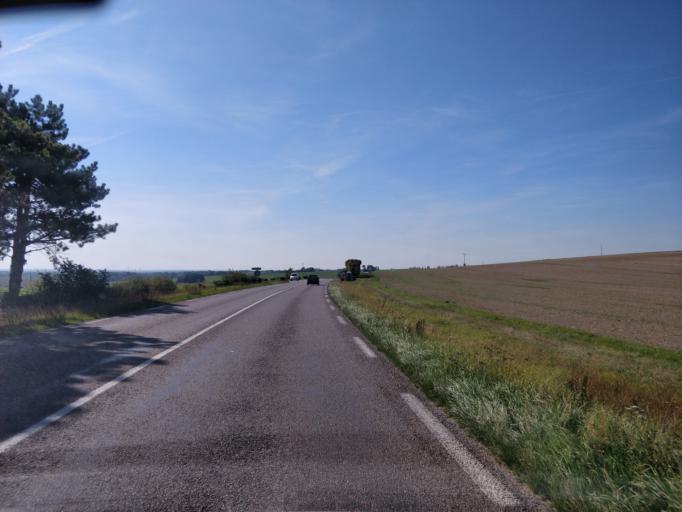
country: FR
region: Champagne-Ardenne
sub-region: Departement de l'Aube
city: Bouilly
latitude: 48.1600
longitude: 4.0230
